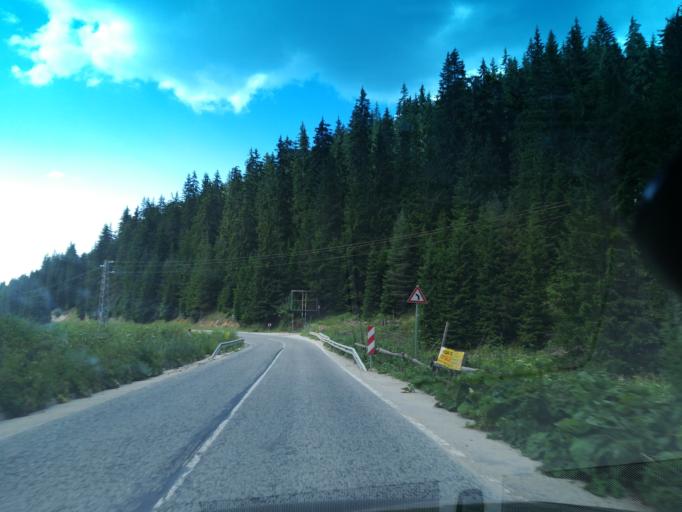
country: BG
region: Smolyan
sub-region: Obshtina Chepelare
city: Chepelare
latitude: 41.6696
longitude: 24.7146
